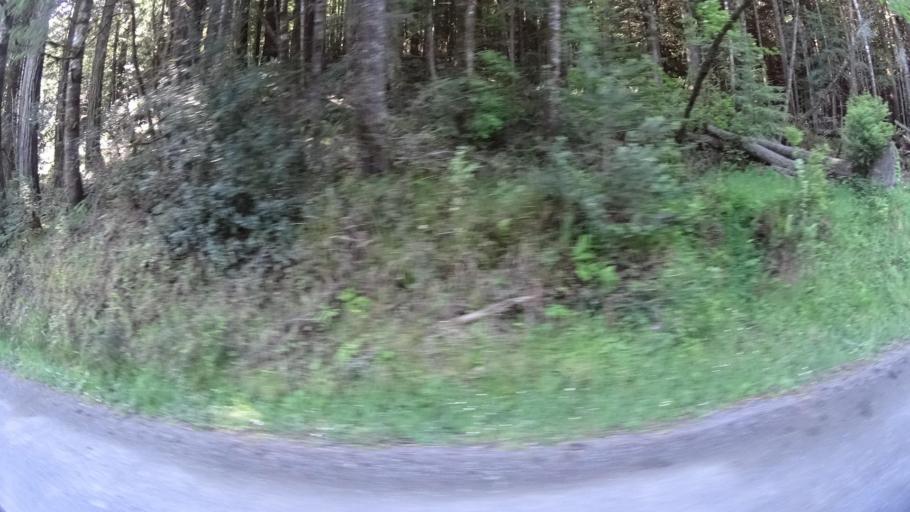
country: US
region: California
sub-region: Humboldt County
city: Fortuna
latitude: 40.5276
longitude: -124.1832
